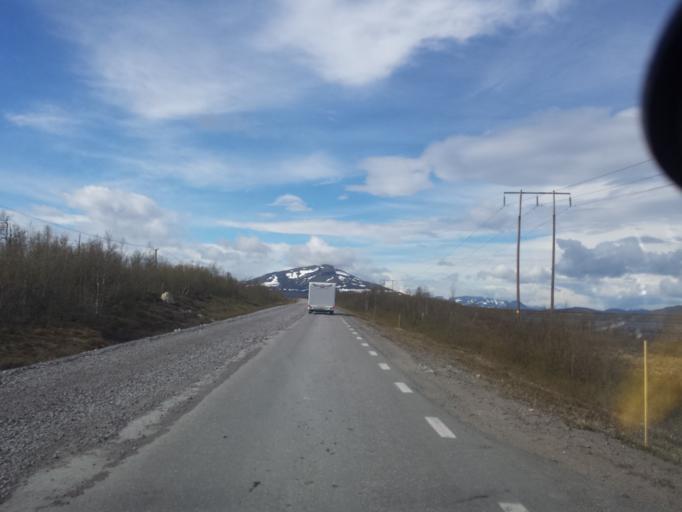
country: SE
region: Norrbotten
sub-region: Kiruna Kommun
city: Kiruna
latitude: 68.1124
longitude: 19.8328
